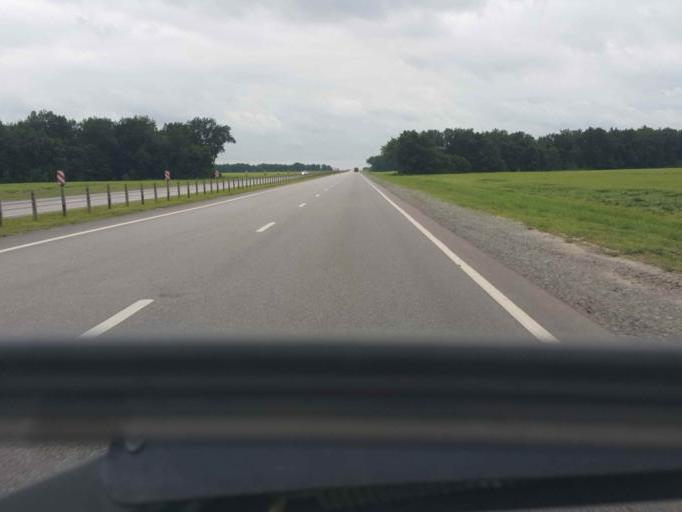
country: RU
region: Tambov
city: Zavoronezhskoye
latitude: 52.8947
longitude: 40.6838
